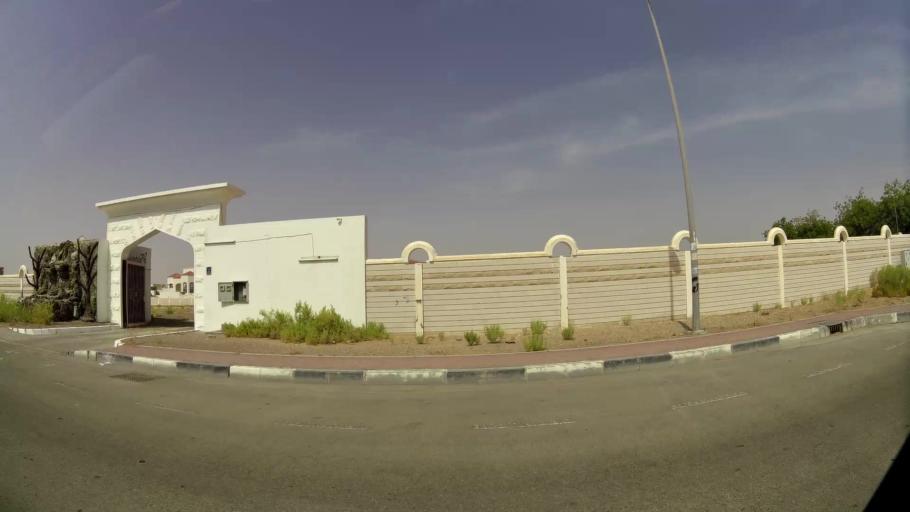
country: AE
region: Abu Dhabi
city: Al Ain
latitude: 24.1608
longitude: 55.6773
